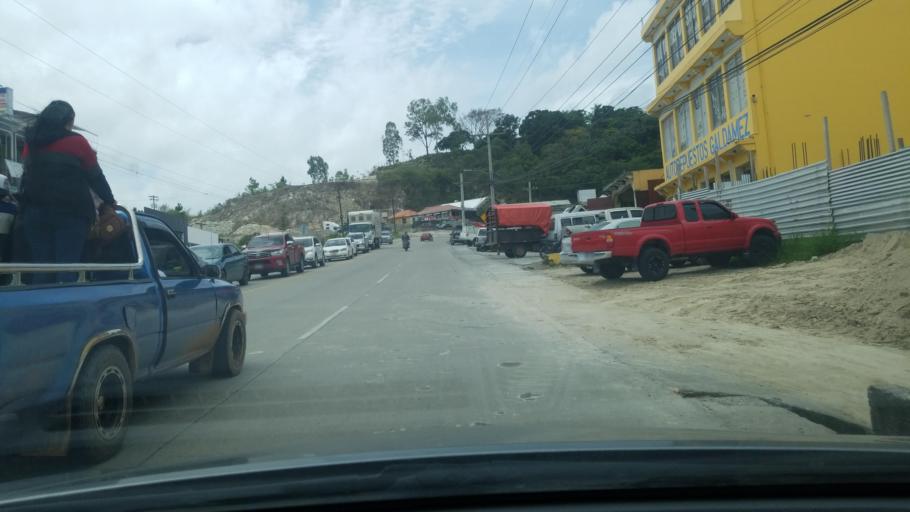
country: HN
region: Copan
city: Santa Rosa de Copan
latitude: 14.7700
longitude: -88.7722
